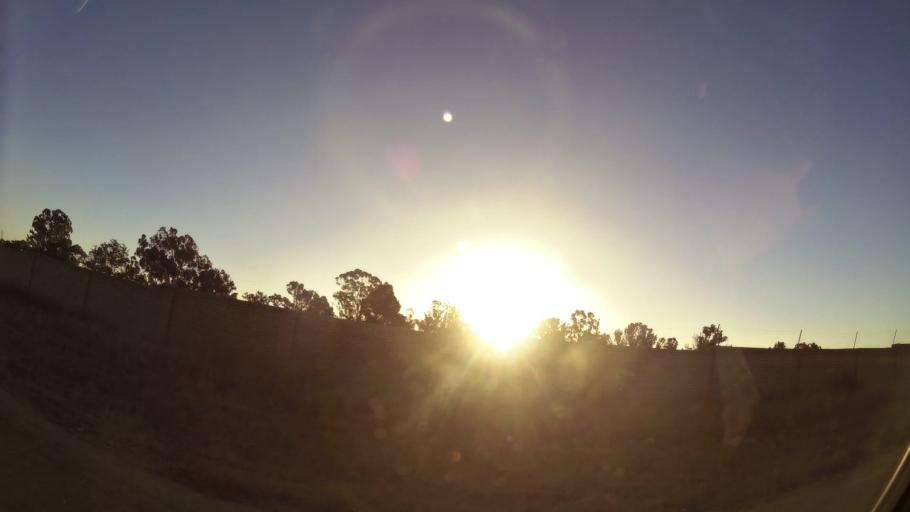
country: ZA
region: Gauteng
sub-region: City of Johannesburg Metropolitan Municipality
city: Diepsloot
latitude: -25.9306
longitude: 28.0391
